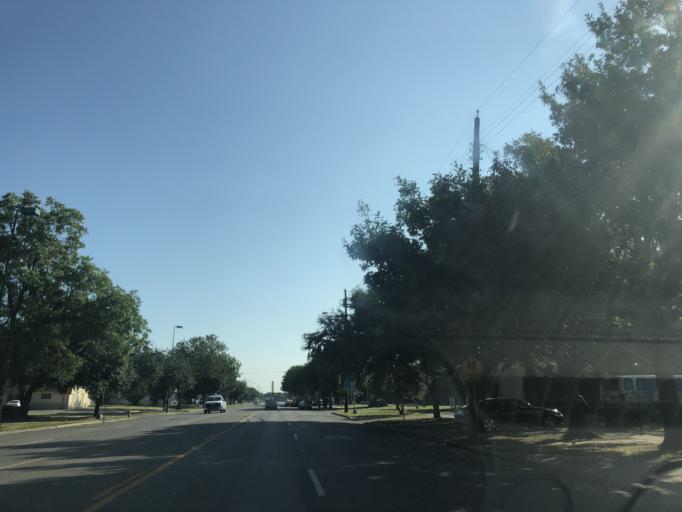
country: US
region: Texas
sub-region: Dallas County
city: Dallas
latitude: 32.7696
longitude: -96.7679
